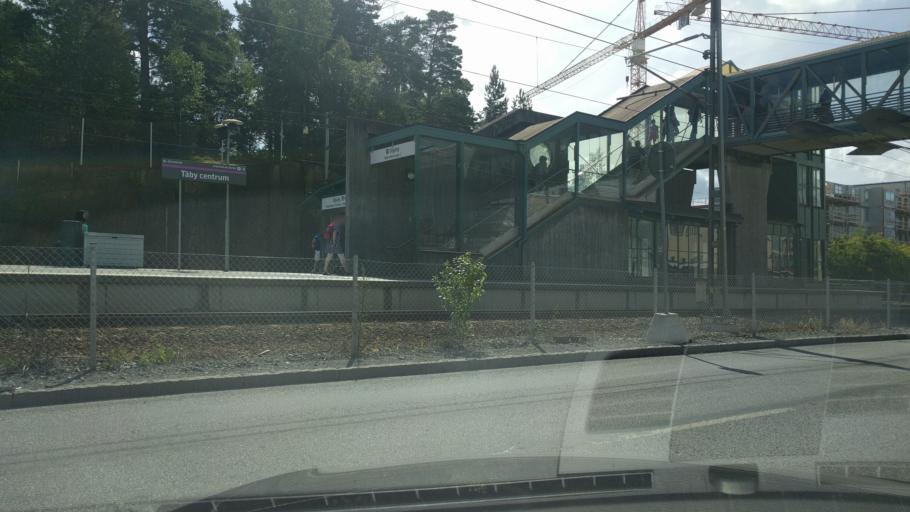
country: SE
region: Stockholm
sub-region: Taby Kommun
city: Taby
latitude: 59.4442
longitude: 18.0739
